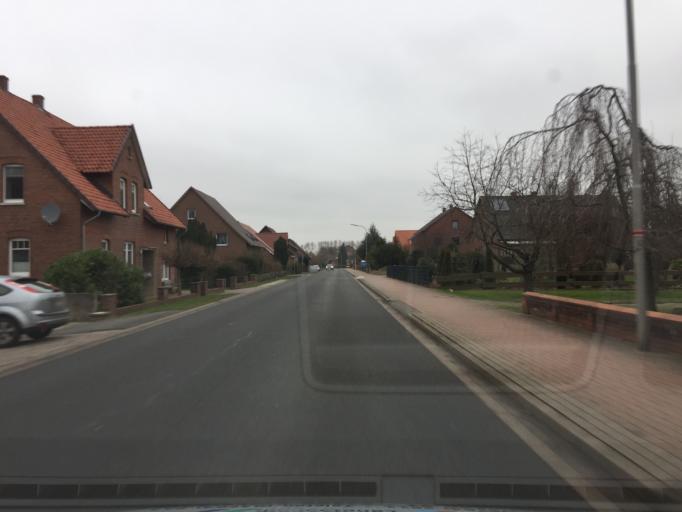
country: DE
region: Lower Saxony
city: Niedernwohren
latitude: 52.3480
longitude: 9.1391
